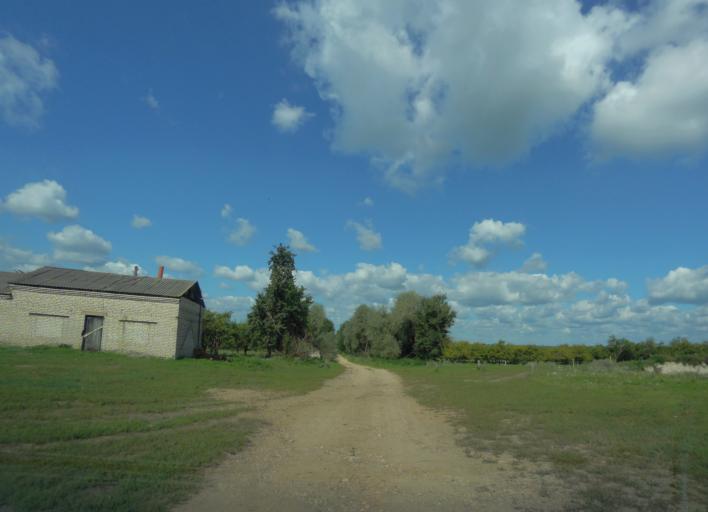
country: BY
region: Minsk
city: Zyembin
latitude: 54.4113
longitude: 28.3820
